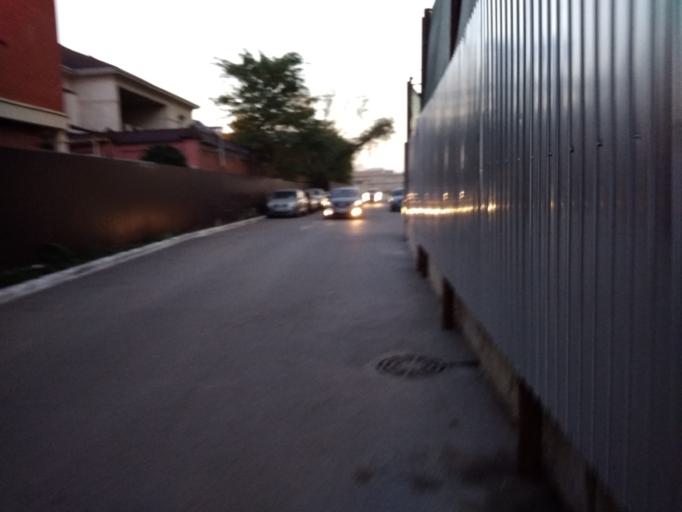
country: RU
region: Krasnodarskiy
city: Krasnodar
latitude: 45.0784
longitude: 39.0040
